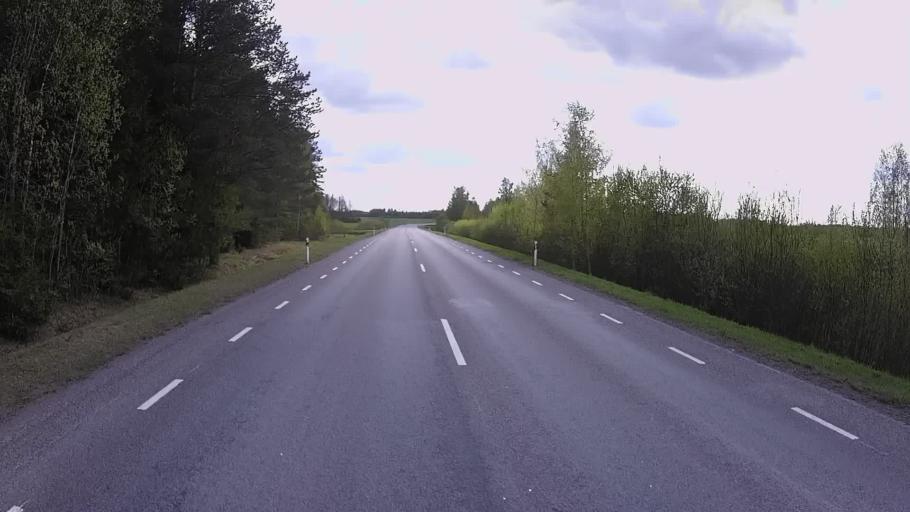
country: EE
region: Tartu
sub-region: Alatskivi vald
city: Kallaste
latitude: 58.5200
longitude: 27.0026
